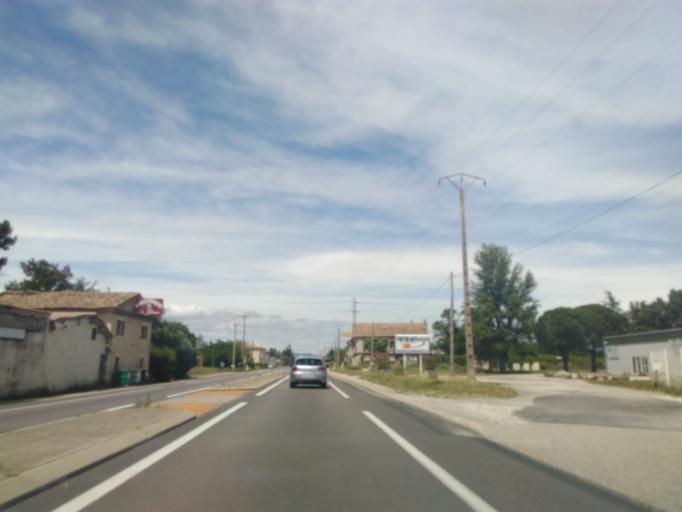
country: FR
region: Rhone-Alpes
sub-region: Departement de la Drome
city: Malataverne
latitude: 44.5158
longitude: 4.7447
